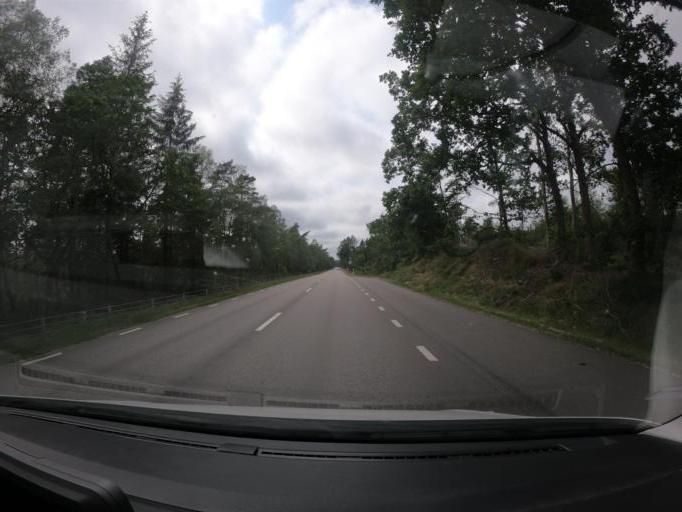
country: SE
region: Skane
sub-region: Perstorps Kommun
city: Perstorp
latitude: 56.2474
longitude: 13.4646
